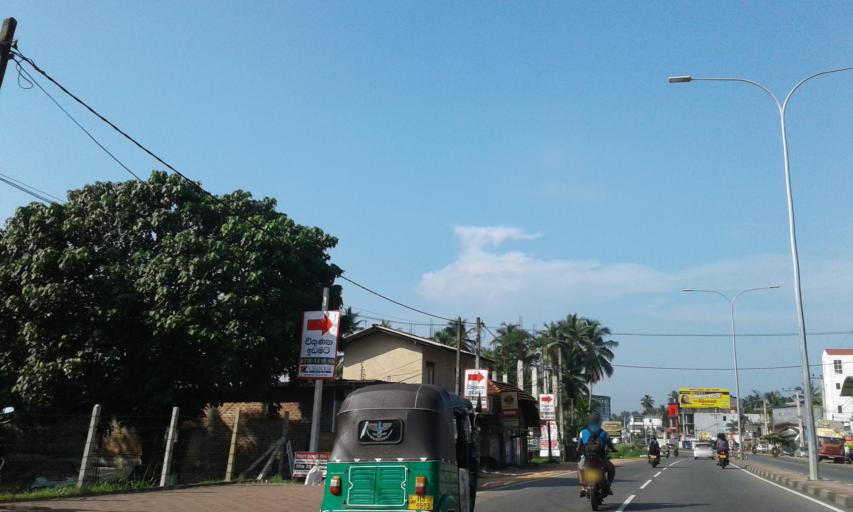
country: LK
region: Western
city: Gampaha
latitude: 7.0344
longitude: 79.9899
